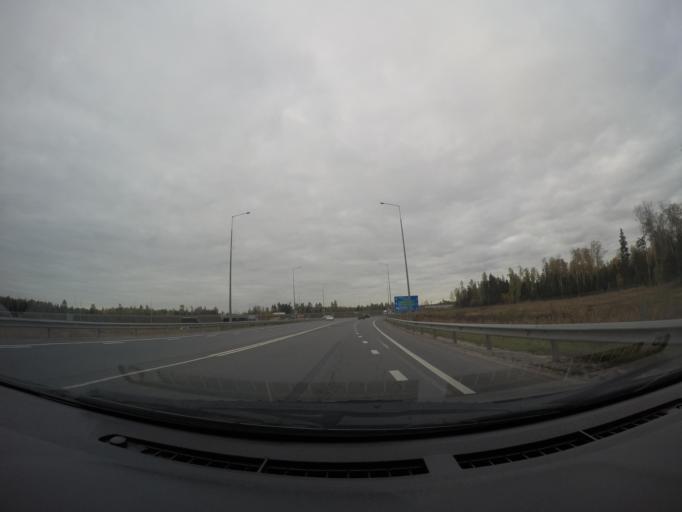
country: RU
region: Moskovskaya
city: Fryazevo
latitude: 55.7000
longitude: 38.4350
